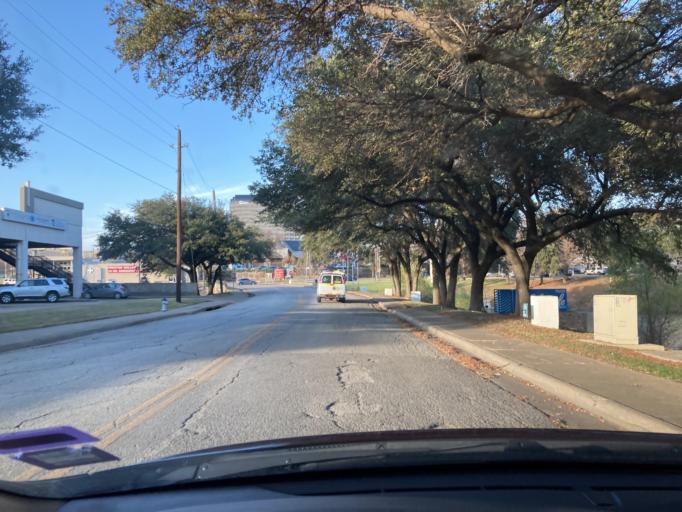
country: US
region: Texas
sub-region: Dallas County
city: University Park
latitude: 32.8789
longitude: -96.7683
